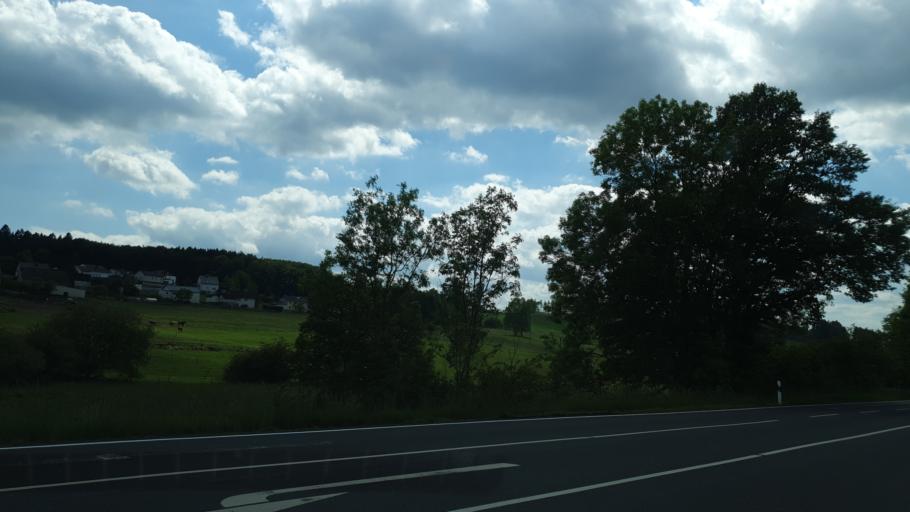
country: DE
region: Rheinland-Pfalz
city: Wolferlingen
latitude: 50.5615
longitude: 7.8576
